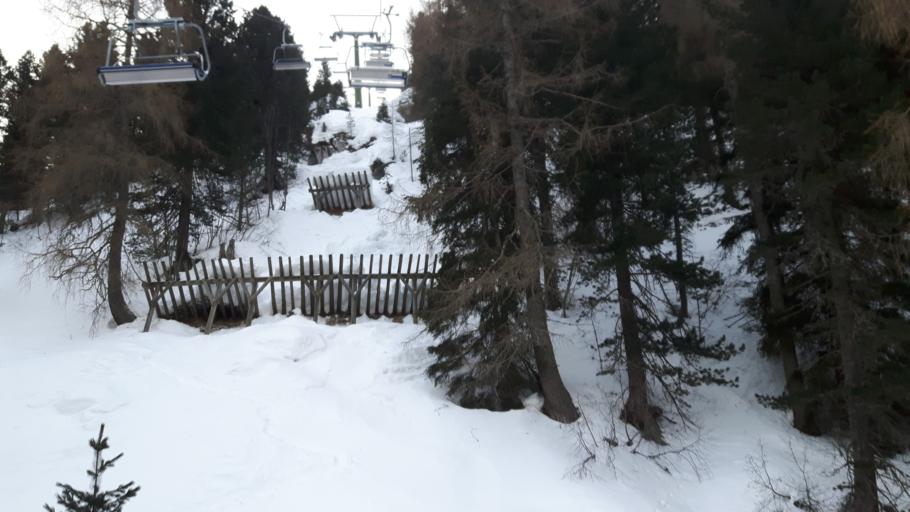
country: IT
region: Trentino-Alto Adige
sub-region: Provincia di Trento
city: Panchia
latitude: 46.3384
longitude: 11.5439
